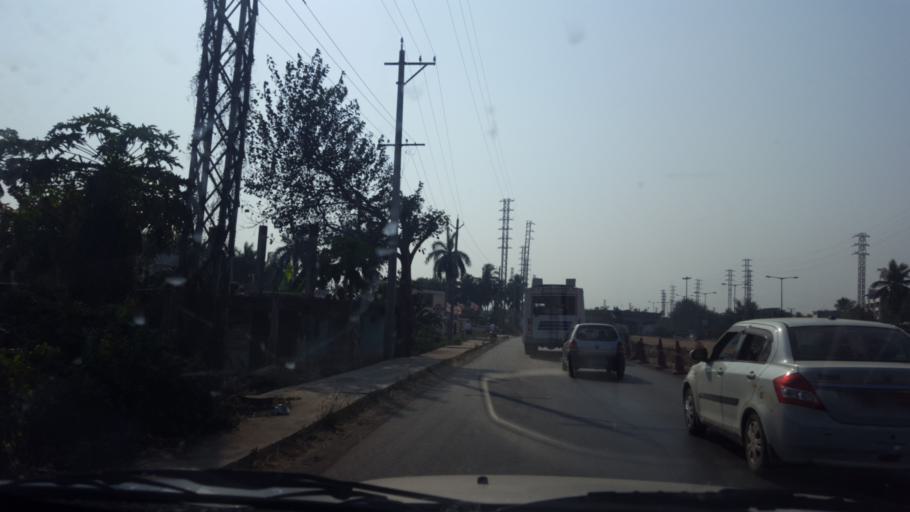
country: IN
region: Andhra Pradesh
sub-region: Vishakhapatnam
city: Anakapalle
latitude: 17.6745
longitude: 83.0035
